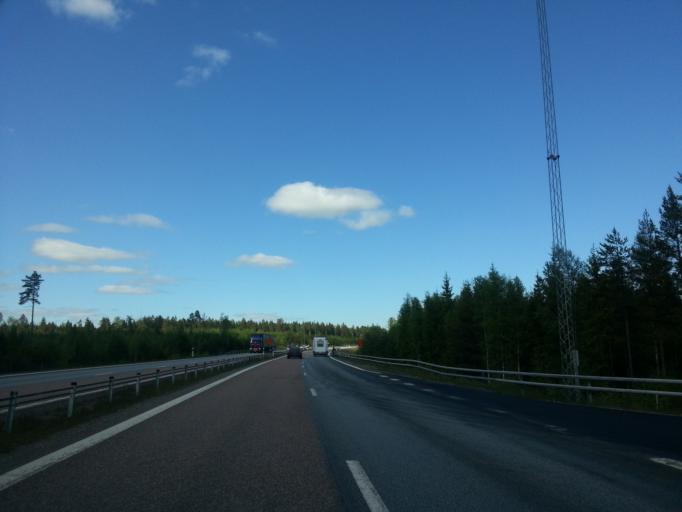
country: SE
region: Gaevleborg
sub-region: Soderhamns Kommun
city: Soderhamn
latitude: 61.4266
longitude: 16.9841
